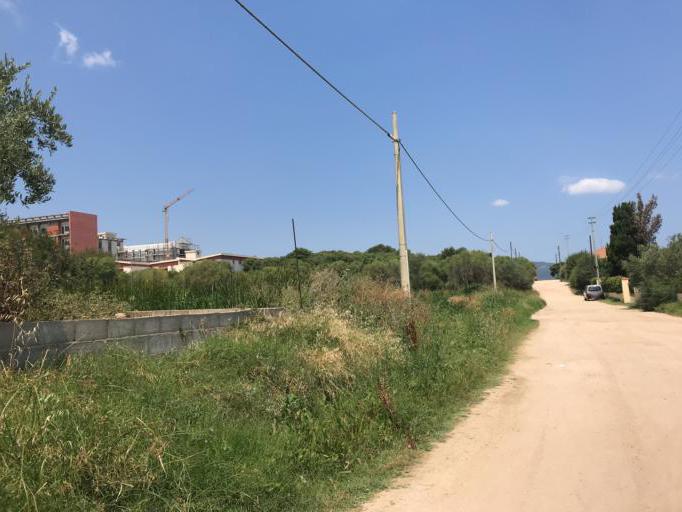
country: IT
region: Sardinia
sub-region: Provincia di Olbia-Tempio
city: Olbia
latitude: 40.9109
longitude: 9.5157
